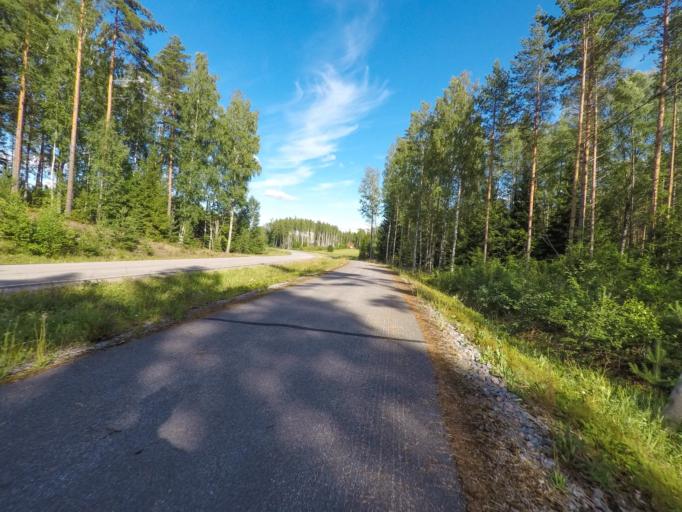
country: FI
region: South Karelia
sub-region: Lappeenranta
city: Joutseno
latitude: 61.1532
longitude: 28.5881
